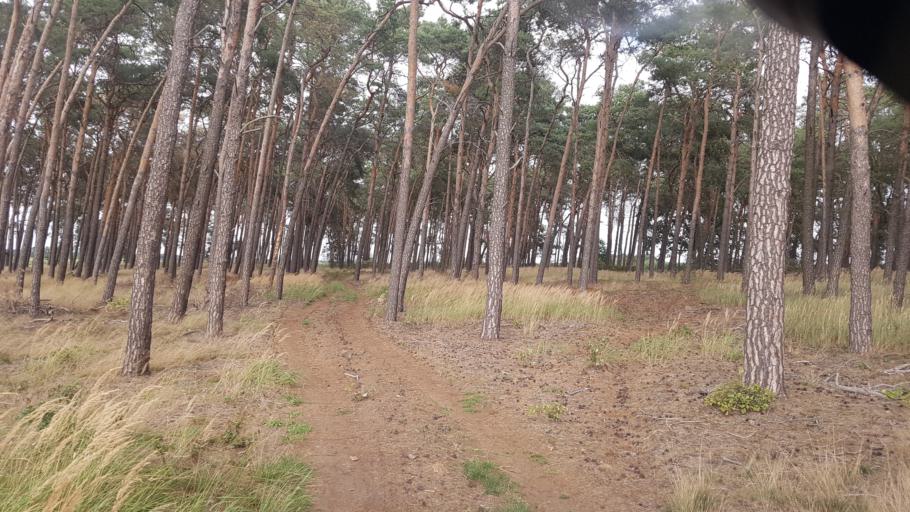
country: DE
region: Brandenburg
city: Schonewalde
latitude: 51.6784
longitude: 13.6248
